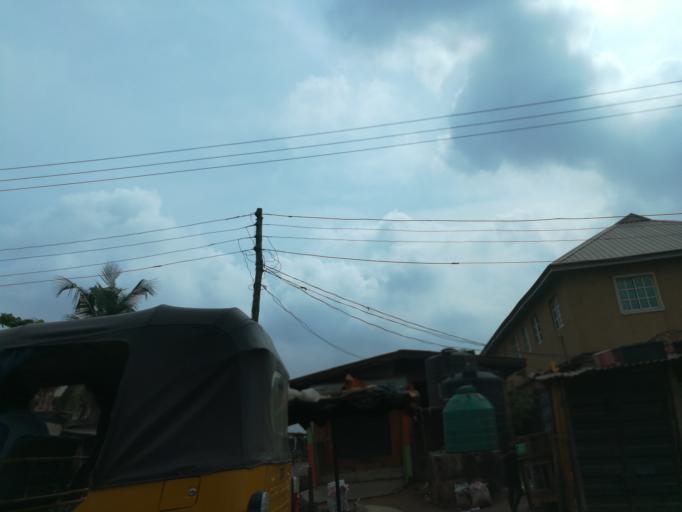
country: NG
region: Lagos
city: Agege
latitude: 6.5852
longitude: 3.3062
